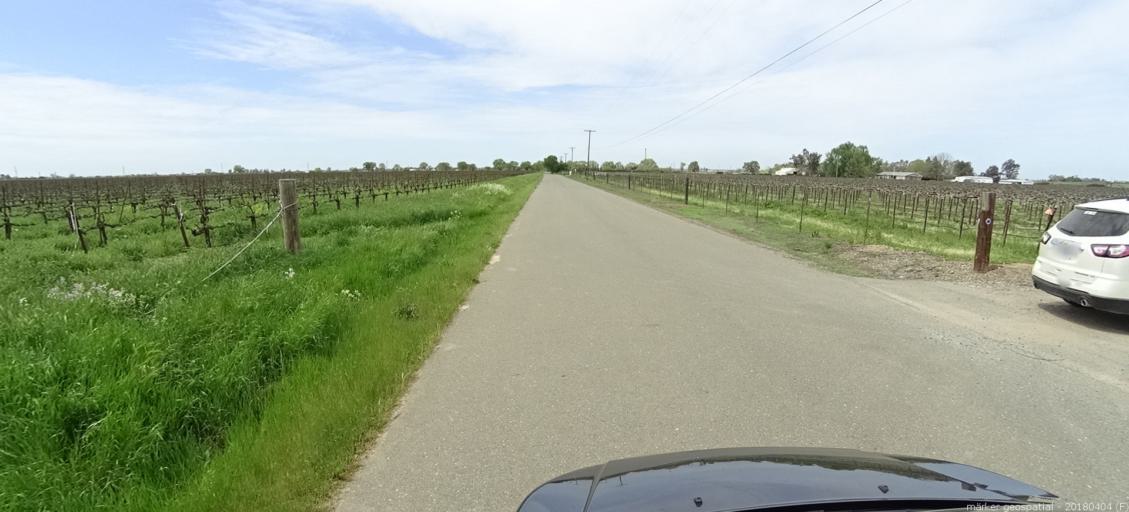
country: US
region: California
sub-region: Sacramento County
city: Clay
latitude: 38.2780
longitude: -121.1804
